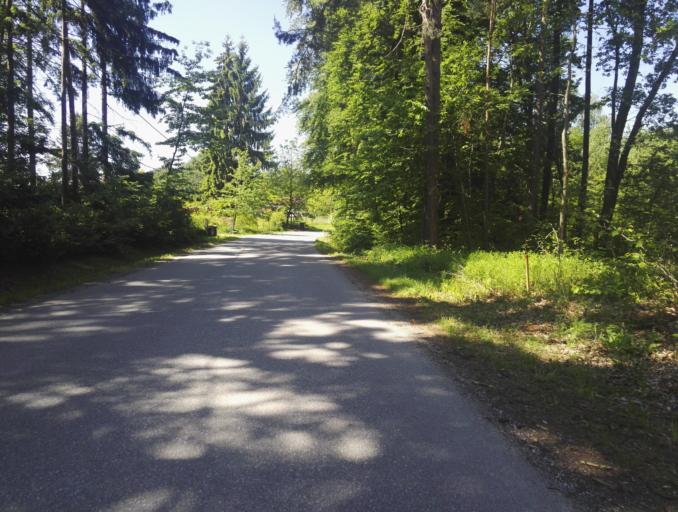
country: AT
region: Styria
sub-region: Politischer Bezirk Graz-Umgebung
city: Edelsgrub
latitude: 47.0511
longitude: 15.5729
